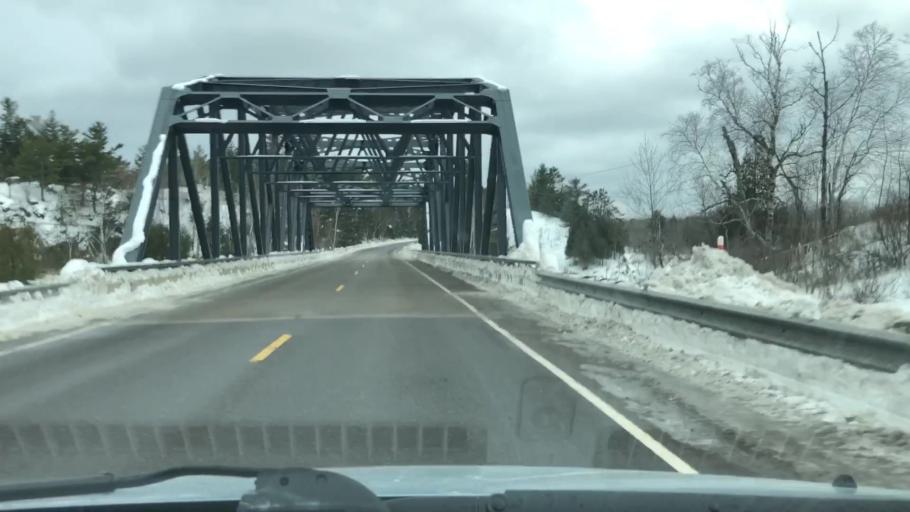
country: US
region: Minnesota
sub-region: Carlton County
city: Carlton
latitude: 46.6648
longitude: -92.4039
